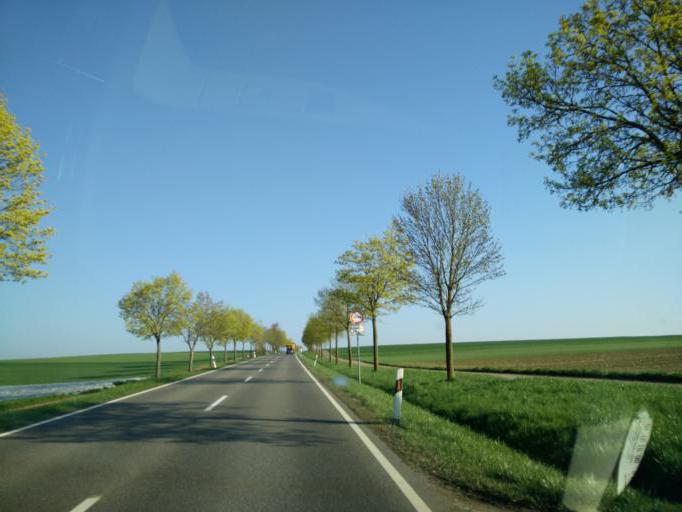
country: DE
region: Baden-Wuerttemberg
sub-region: Regierungsbezirk Stuttgart
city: Deckenpfronn
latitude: 48.6302
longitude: 8.8301
